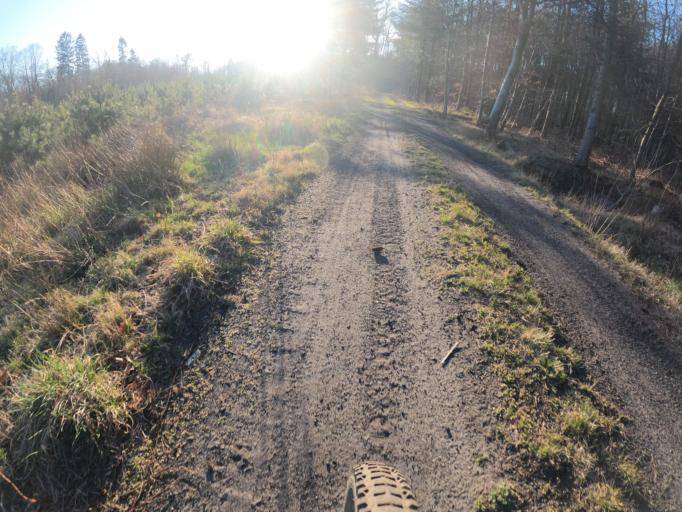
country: PL
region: West Pomeranian Voivodeship
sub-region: Powiat gryficki
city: Brojce
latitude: 53.9600
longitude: 15.3762
